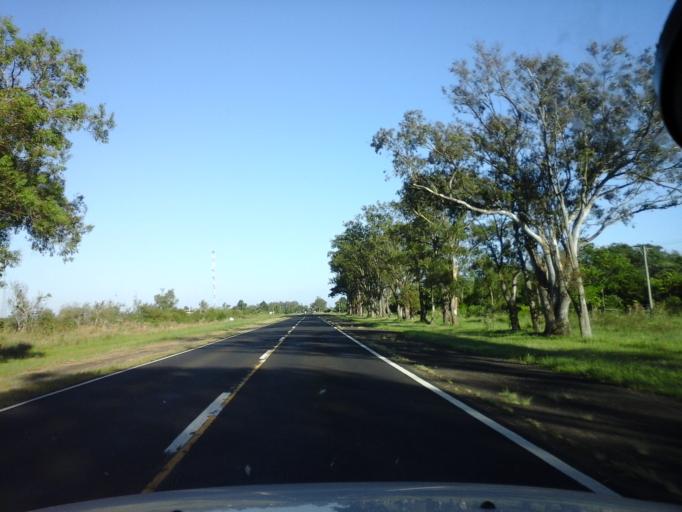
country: AR
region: Corrientes
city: Ita Ibate
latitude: -27.4496
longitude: -57.3307
